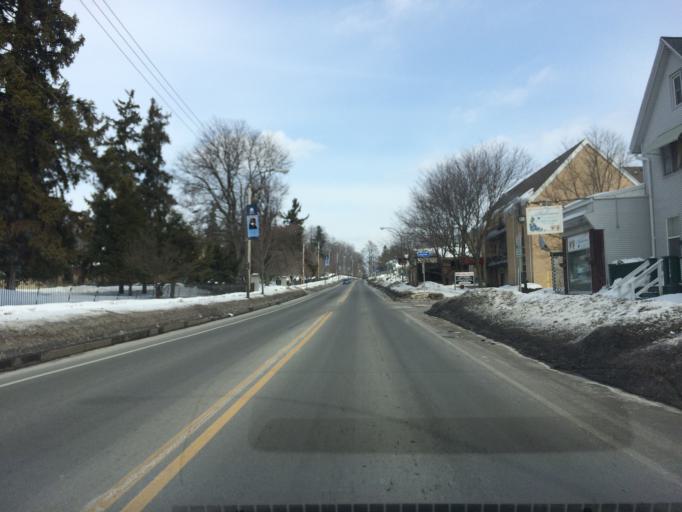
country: US
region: New York
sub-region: Monroe County
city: Rochester
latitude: 43.1269
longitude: -77.6163
